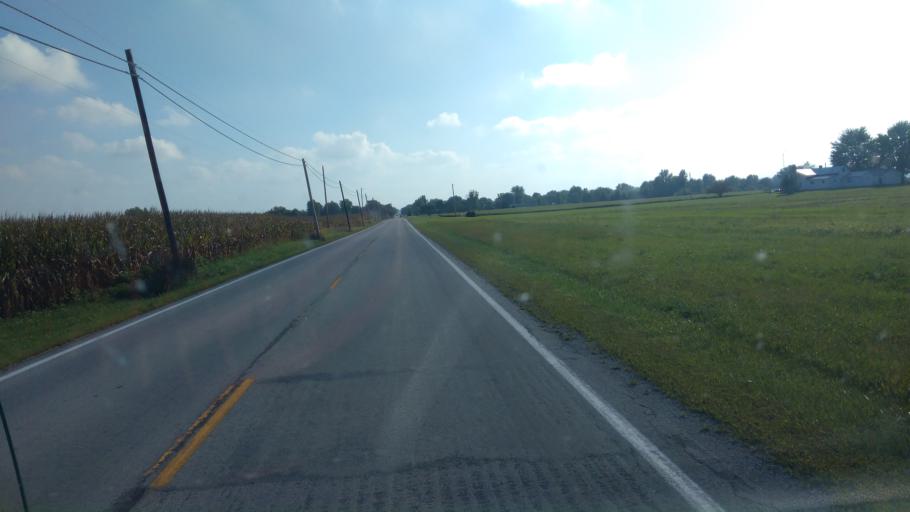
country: US
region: Ohio
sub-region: Hardin County
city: Forest
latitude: 40.7880
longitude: -83.5212
